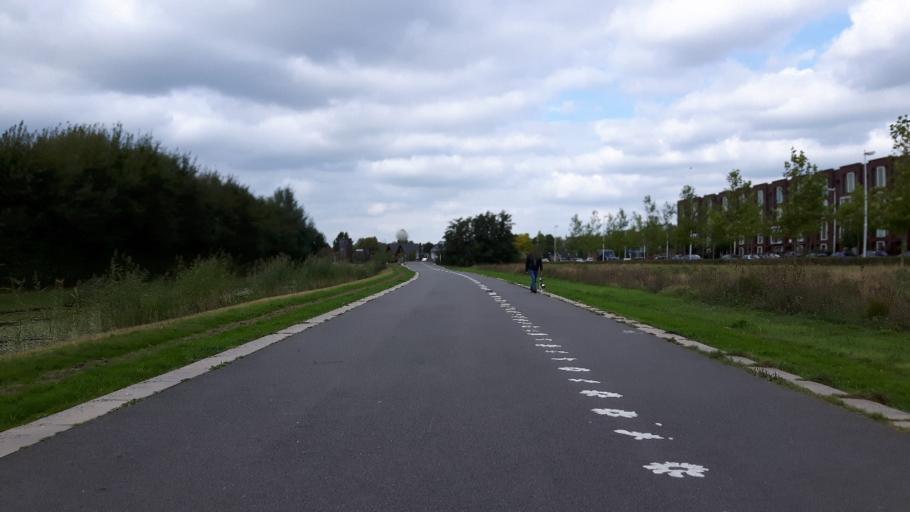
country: NL
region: Utrecht
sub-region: Stichtse Vecht
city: Maarssen
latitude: 52.0959
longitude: 5.0356
